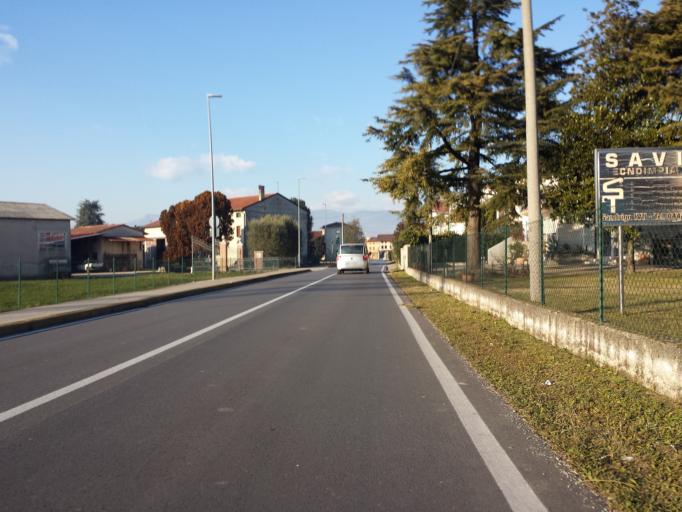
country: IT
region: Veneto
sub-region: Provincia di Vicenza
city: Sandrigo
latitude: 45.6499
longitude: 11.6052
